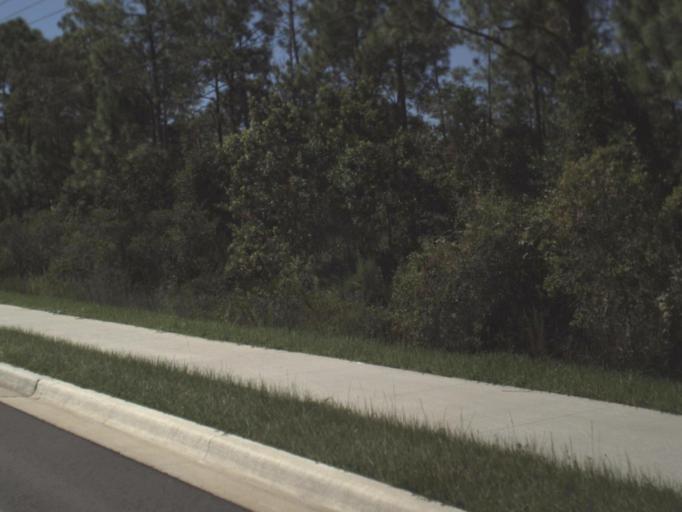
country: US
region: Florida
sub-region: Collier County
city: Golden Gate
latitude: 26.1454
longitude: -81.7038
